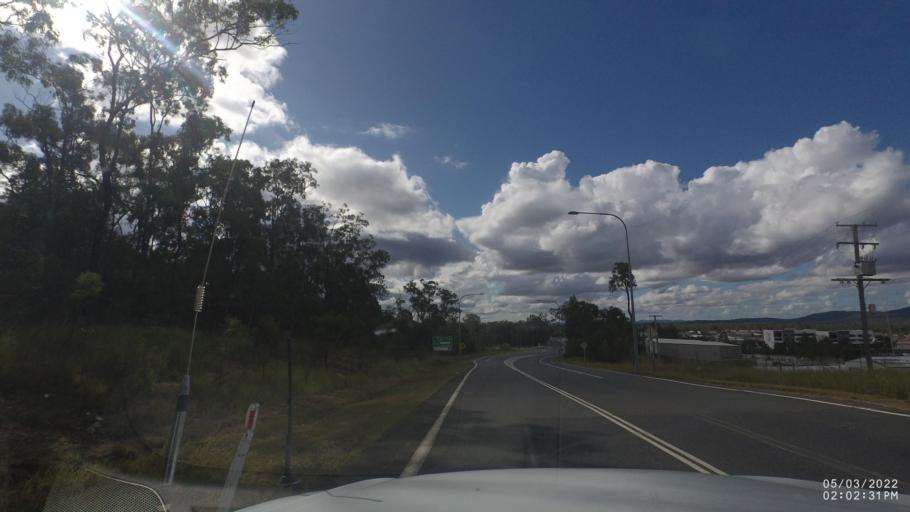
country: AU
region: Queensland
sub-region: Logan
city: Chambers Flat
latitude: -27.8034
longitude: 153.0986
